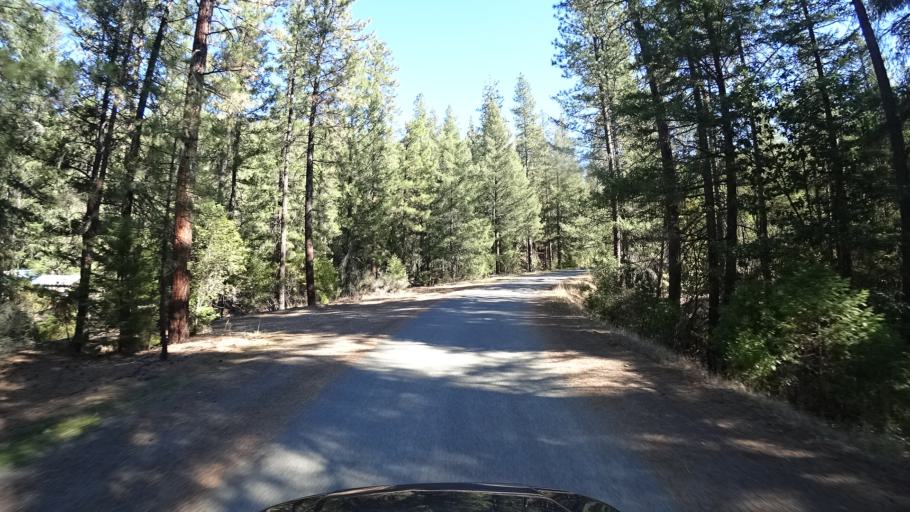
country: US
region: California
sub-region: Trinity County
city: Weaverville
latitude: 41.1400
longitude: -123.1293
